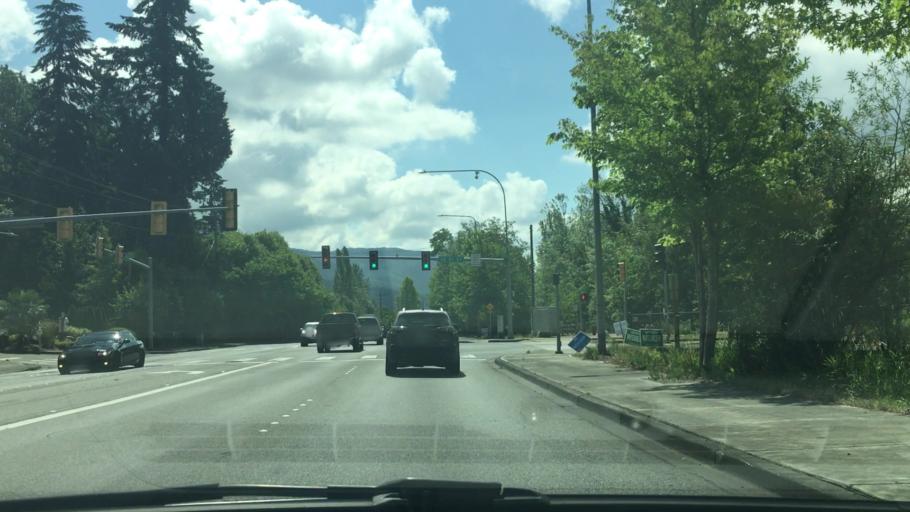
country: US
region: Washington
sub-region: King County
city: Issaquah
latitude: 47.5570
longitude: -122.0466
